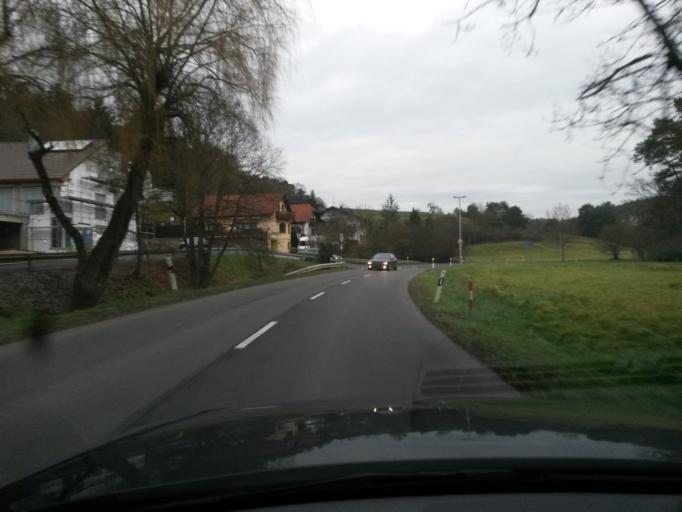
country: DE
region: Bavaria
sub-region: Regierungsbezirk Unterfranken
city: Gadheim
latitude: 49.8224
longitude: 9.9179
